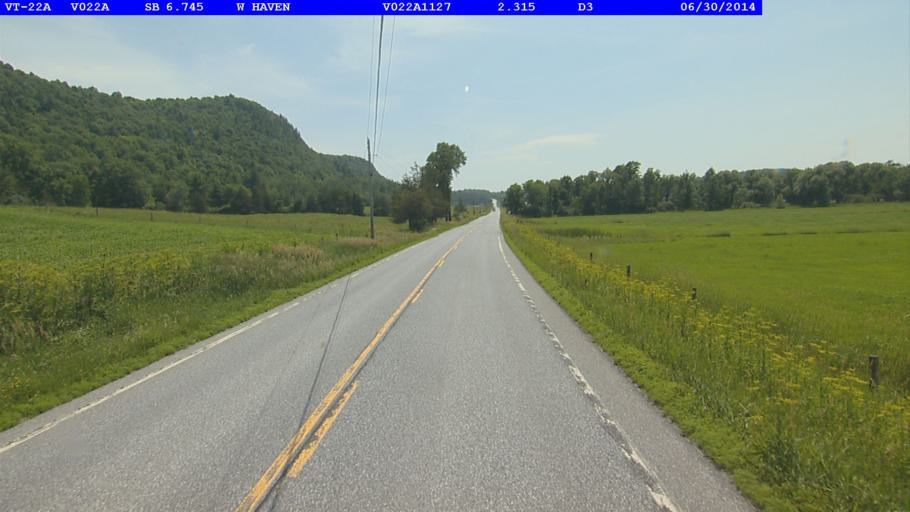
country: US
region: Vermont
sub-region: Rutland County
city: Fair Haven
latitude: 43.6598
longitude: -73.2914
